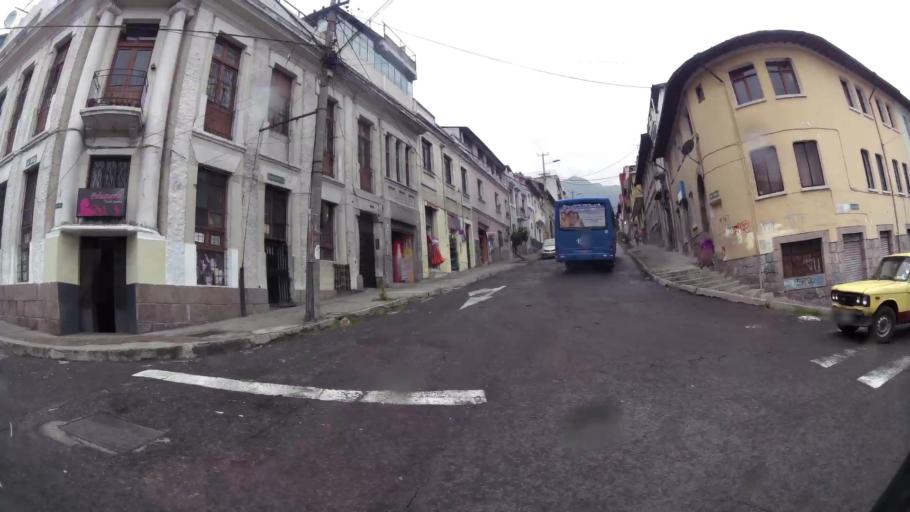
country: EC
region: Pichincha
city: Quito
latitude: -0.2136
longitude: -78.5063
